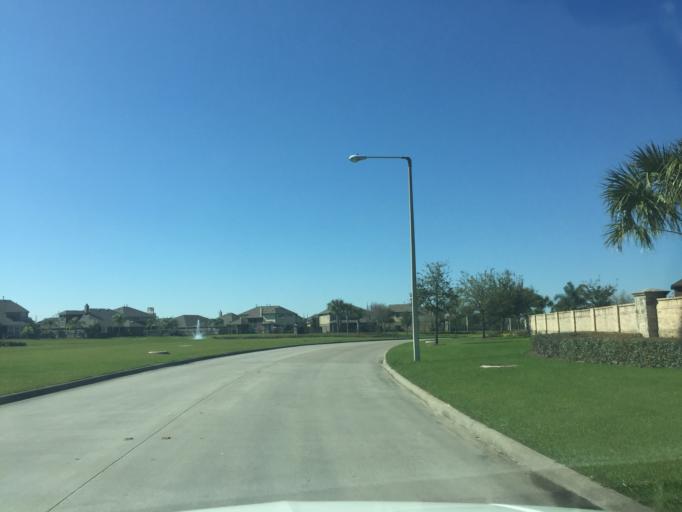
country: US
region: Texas
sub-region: Galveston County
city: Kemah
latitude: 29.5146
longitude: -95.0214
